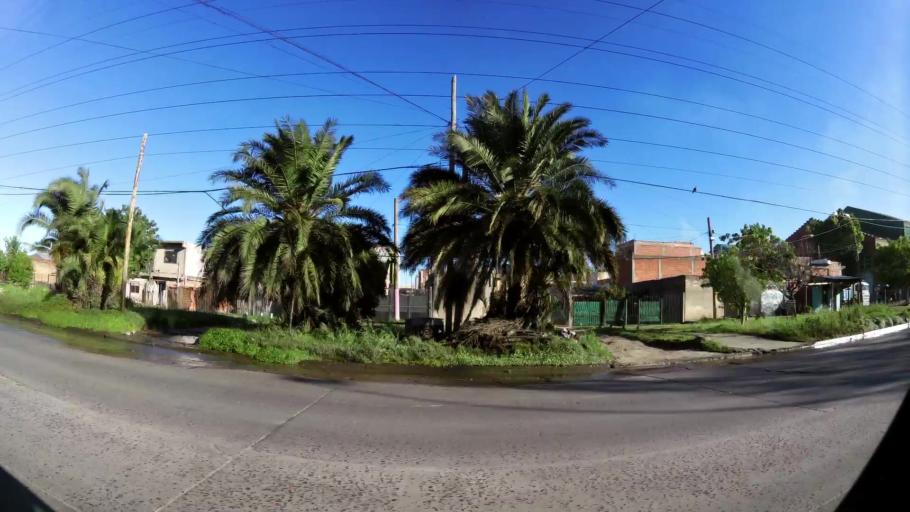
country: AR
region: Buenos Aires
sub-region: Partido de Almirante Brown
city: Adrogue
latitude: -34.7482
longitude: -58.3342
